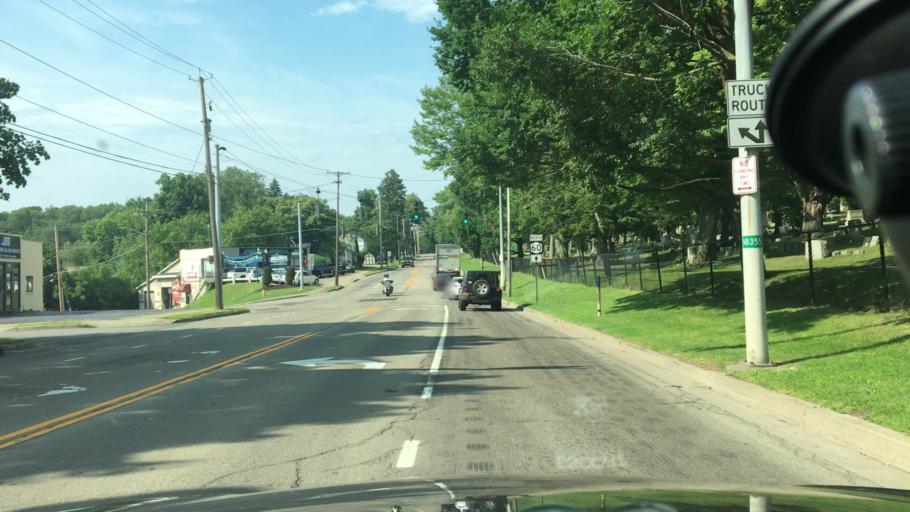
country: US
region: New York
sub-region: Chautauqua County
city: Jamestown
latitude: 42.1111
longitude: -79.2409
